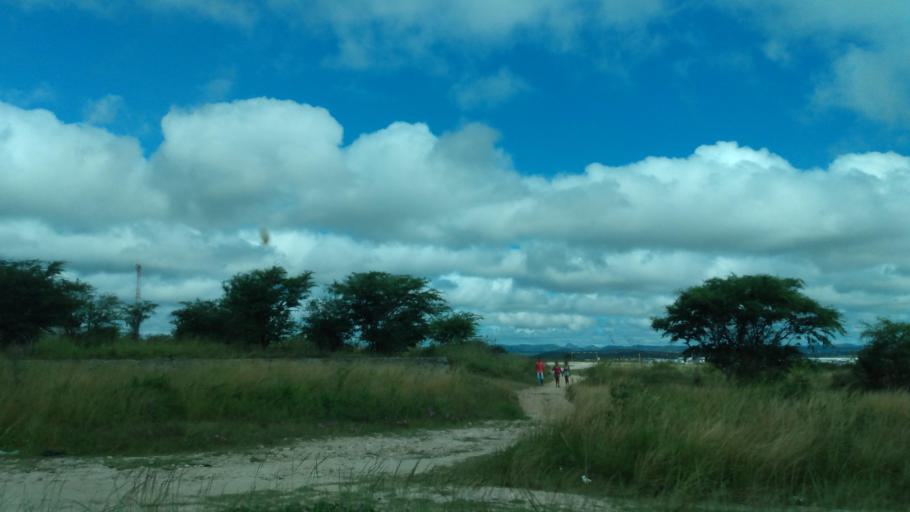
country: BR
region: Pernambuco
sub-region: Caruaru
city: Caruaru
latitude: -8.3067
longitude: -35.9896
